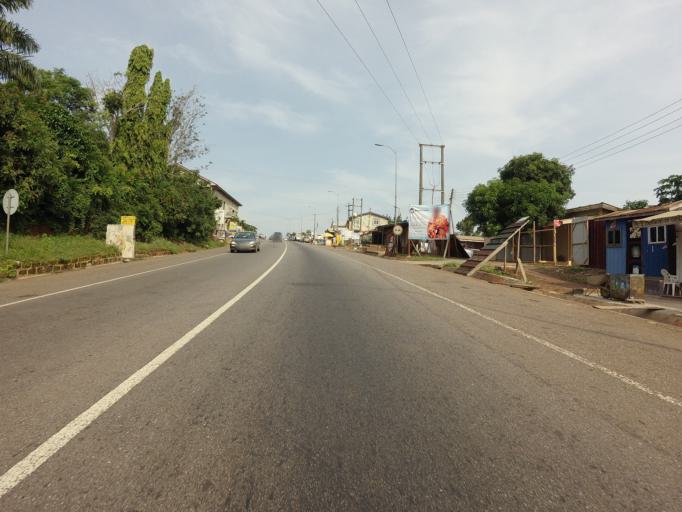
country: GH
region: Eastern
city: Aburi
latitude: 5.8122
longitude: -0.1852
